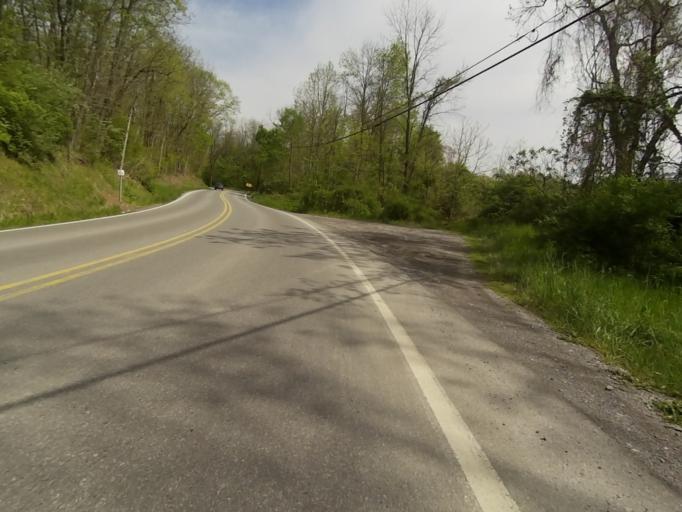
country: US
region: Pennsylvania
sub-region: Centre County
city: Zion
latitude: 40.9896
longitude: -77.6423
